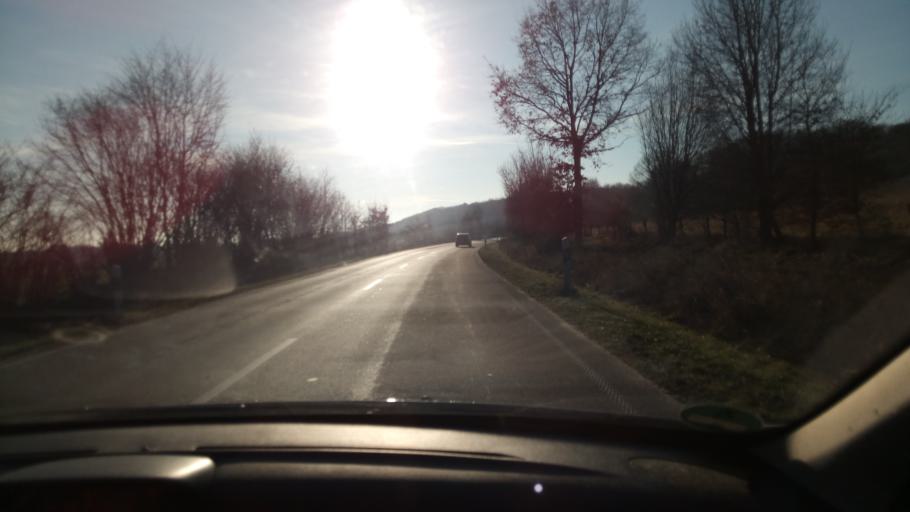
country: DE
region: Schleswig-Holstein
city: Dalldorf
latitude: 53.4313
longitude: 10.6014
